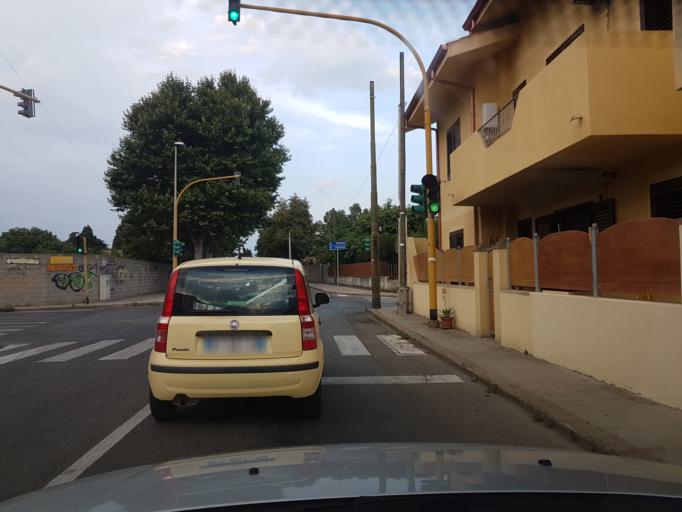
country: IT
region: Sardinia
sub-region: Provincia di Oristano
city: Cabras
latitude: 39.9293
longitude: 8.5382
